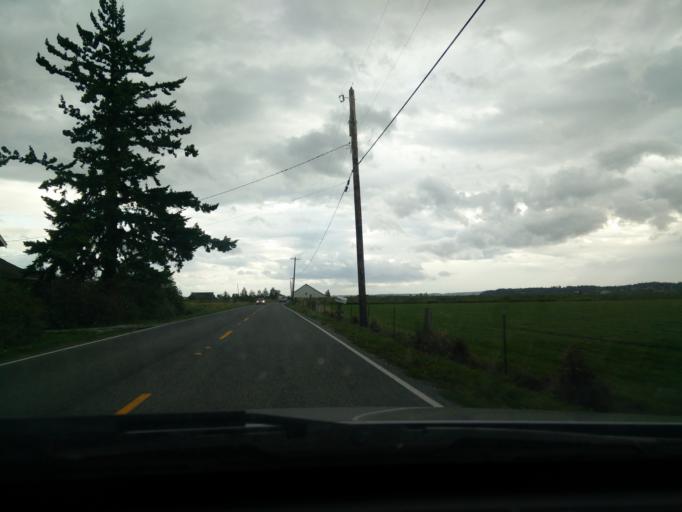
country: US
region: Washington
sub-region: Snohomish County
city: Stanwood
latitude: 48.2643
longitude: -122.3685
